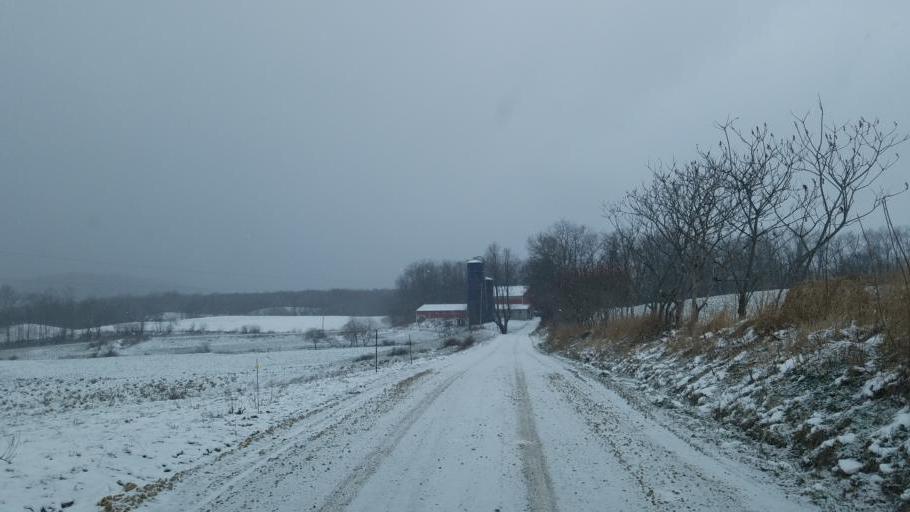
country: US
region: Pennsylvania
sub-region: Venango County
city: Sugarcreek
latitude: 41.4571
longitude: -79.9602
